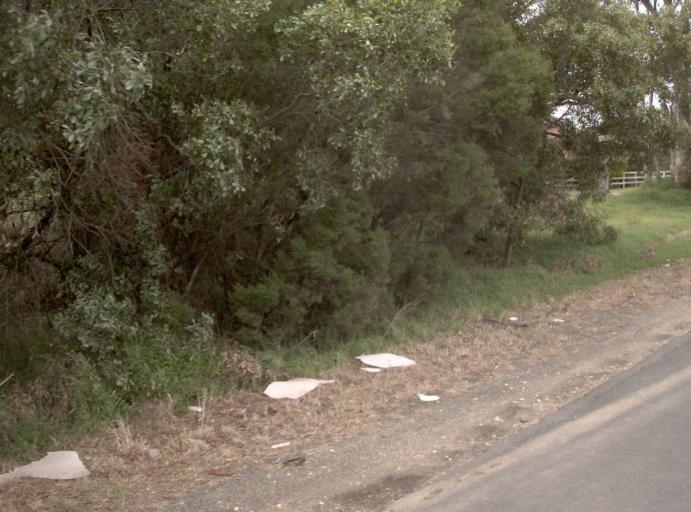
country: AU
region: Victoria
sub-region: Wellington
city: Sale
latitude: -37.9805
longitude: 147.0724
